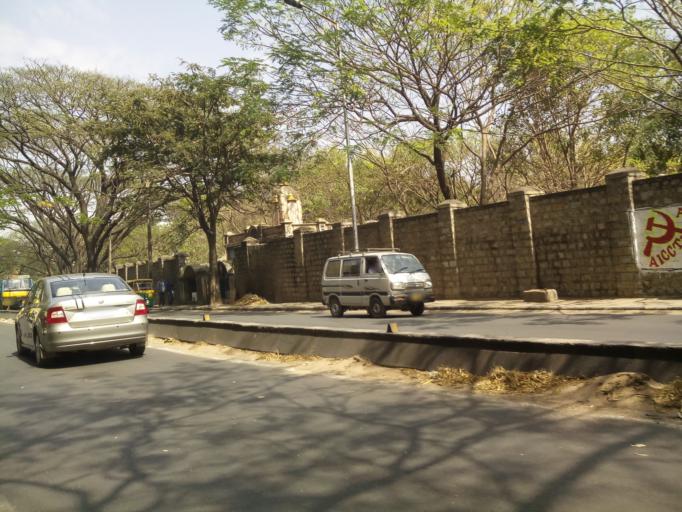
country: IN
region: Karnataka
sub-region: Bangalore Urban
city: Bangalore
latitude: 12.9817
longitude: 77.6316
